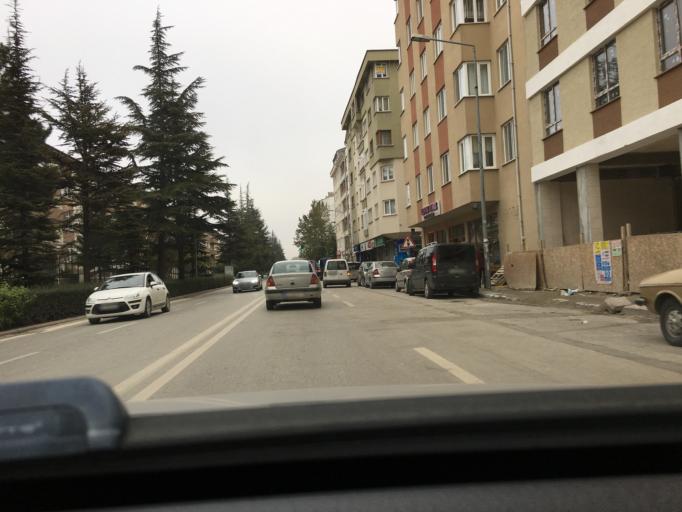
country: TR
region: Eskisehir
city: Eskisehir
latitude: 39.7725
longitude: 30.4919
